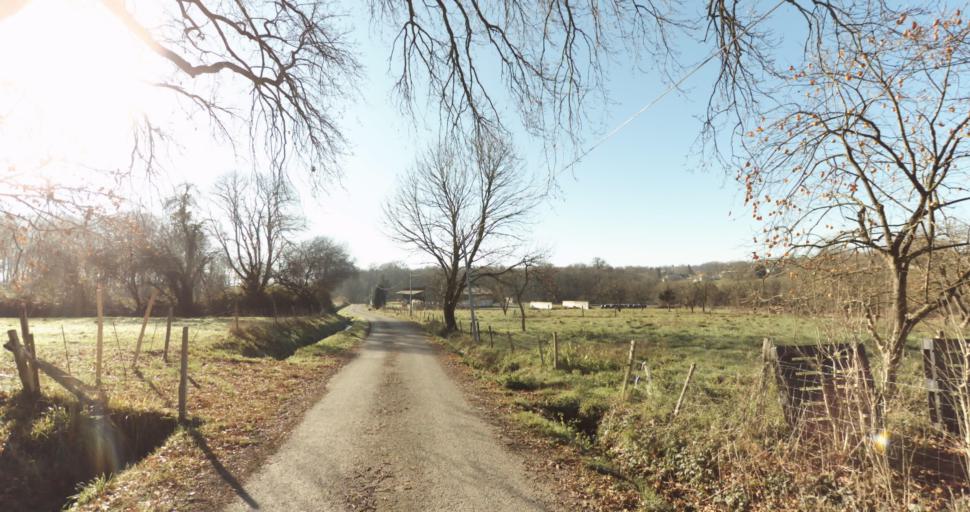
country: FR
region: Aquitaine
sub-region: Departement des Pyrenees-Atlantiques
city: Morlaas
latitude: 43.3430
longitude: -0.2442
